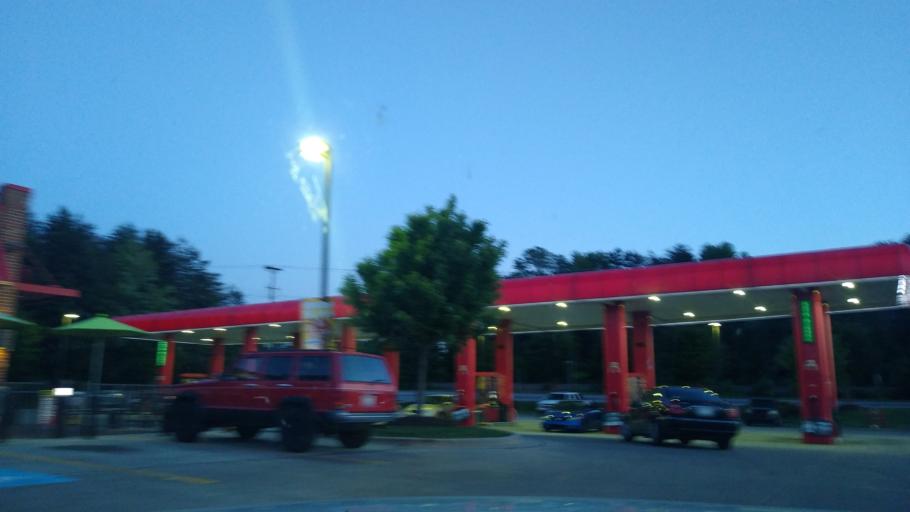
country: US
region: North Carolina
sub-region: Guilford County
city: Jamestown
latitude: 36.0815
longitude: -79.9306
